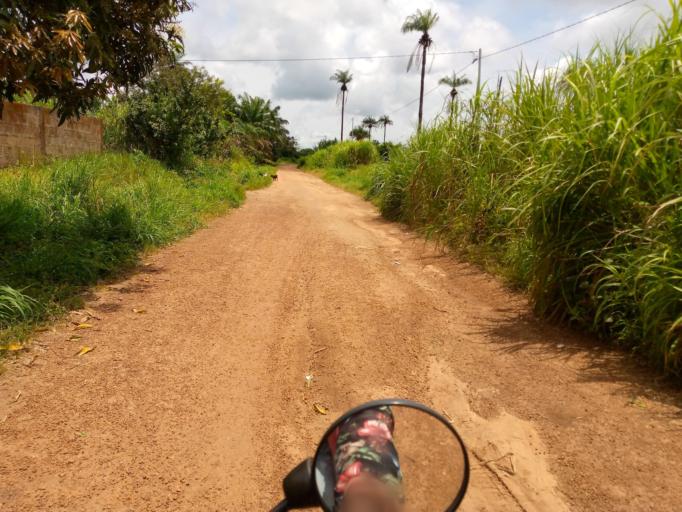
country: SL
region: Northern Province
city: Binkolo
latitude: 9.1112
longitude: -12.1976
